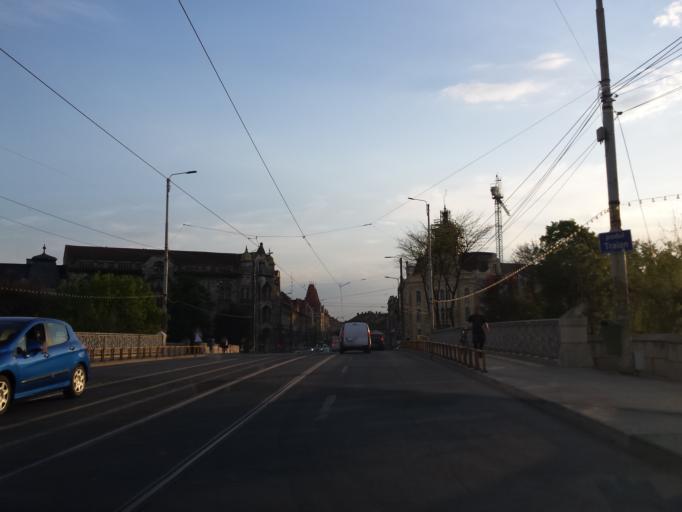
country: RO
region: Timis
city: Timisoara
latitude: 45.7499
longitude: 21.2212
